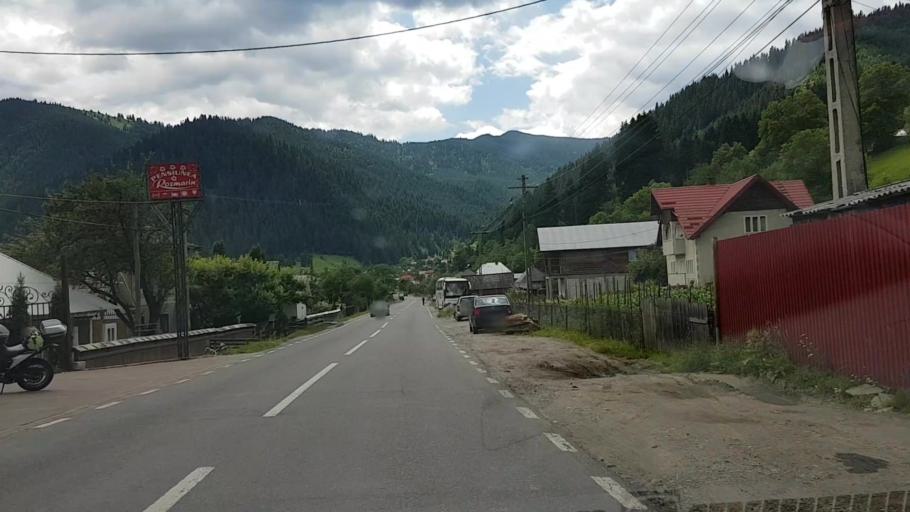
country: RO
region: Neamt
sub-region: Comuna Borca
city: Borca
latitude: 47.2096
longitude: 25.7547
